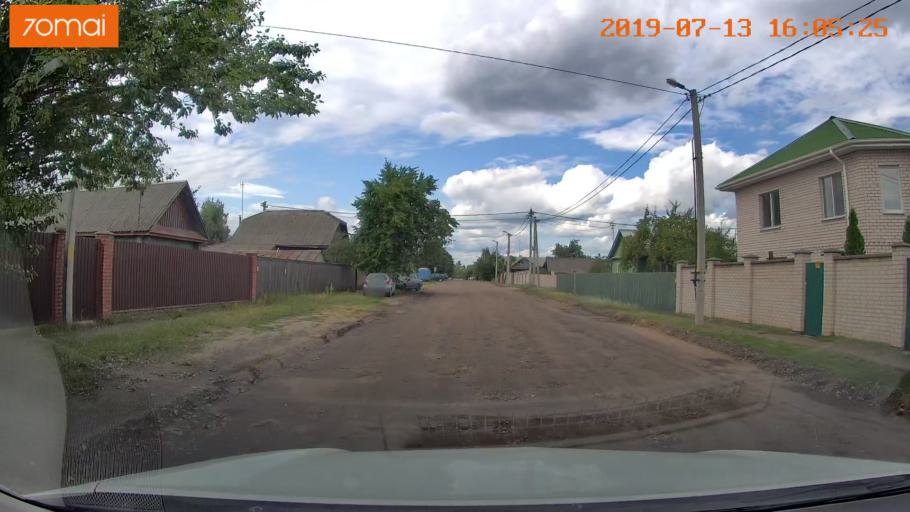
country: BY
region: Mogilev
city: Babruysk
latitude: 53.1485
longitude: 29.2052
